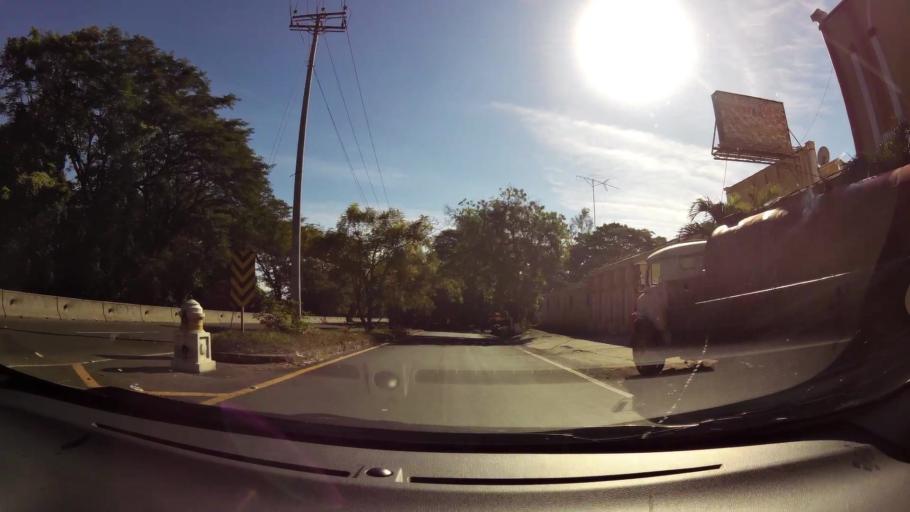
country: SV
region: Santa Ana
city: Santa Ana
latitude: 13.9552
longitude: -89.5704
